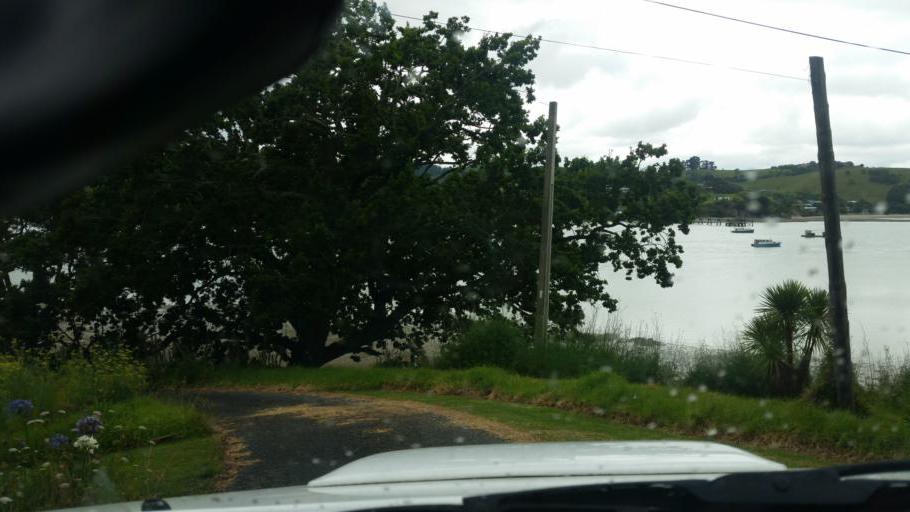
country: NZ
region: Auckland
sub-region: Auckland
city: Wellsford
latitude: -36.1549
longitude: 174.2277
